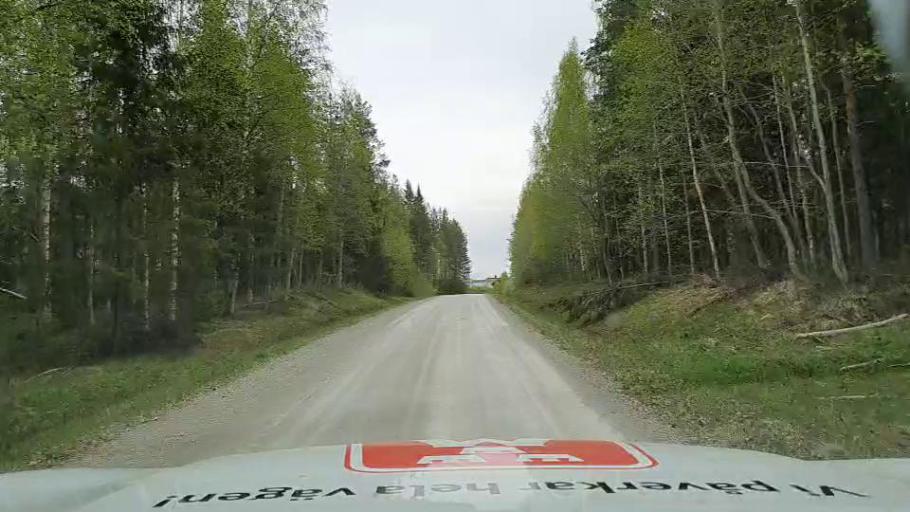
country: SE
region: Jaemtland
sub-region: Bergs Kommun
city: Hoverberg
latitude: 62.6851
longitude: 14.7746
